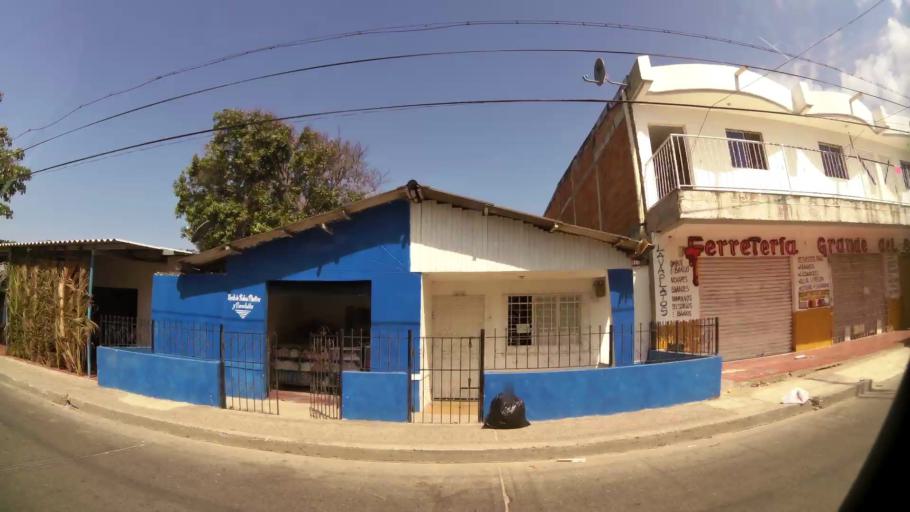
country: CO
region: Atlantico
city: Barranquilla
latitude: 10.9638
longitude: -74.8288
